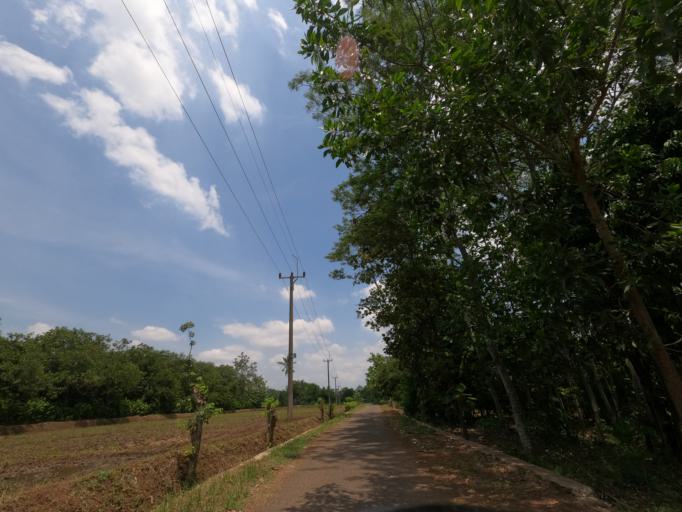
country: ID
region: West Java
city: Pamanukan
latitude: -6.5081
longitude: 107.7706
